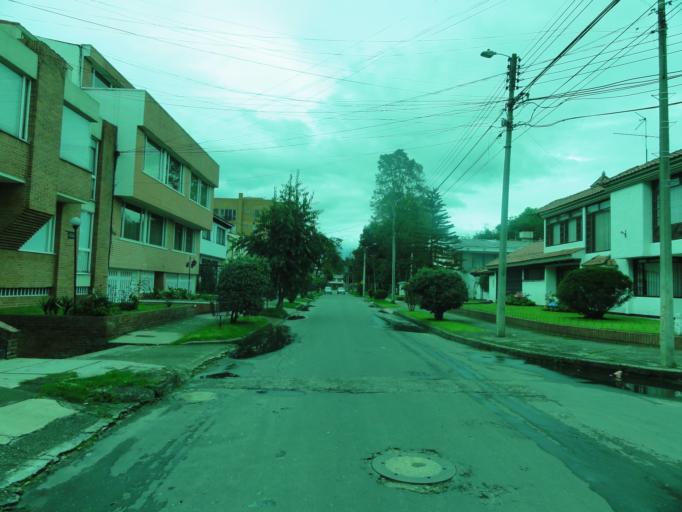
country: CO
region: Bogota D.C.
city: Bogota
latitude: 4.6492
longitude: -74.0845
